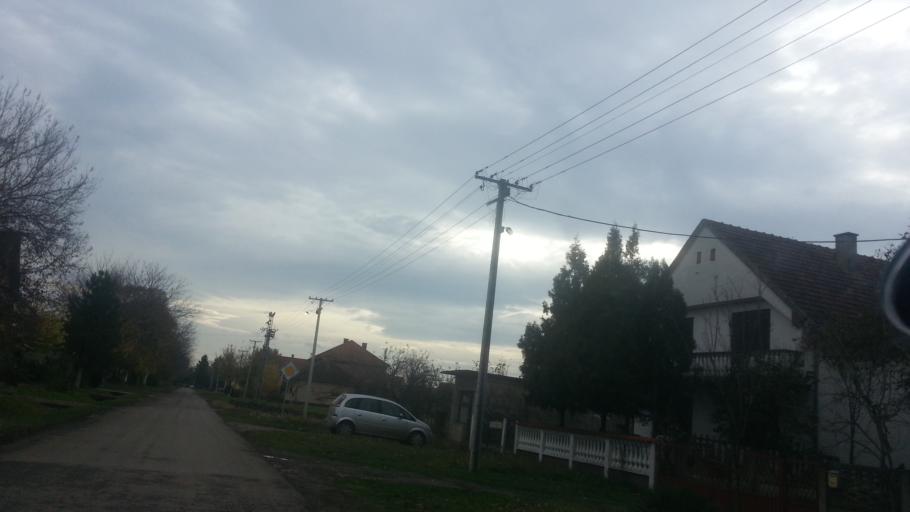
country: RS
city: Golubinci
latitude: 44.9931
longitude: 20.0578
